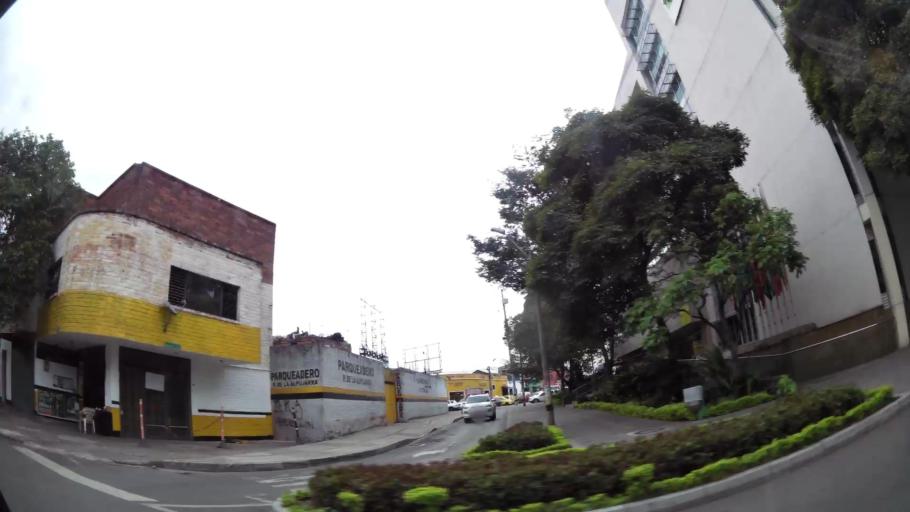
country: CO
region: Antioquia
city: Medellin
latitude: 6.2424
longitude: -75.5738
